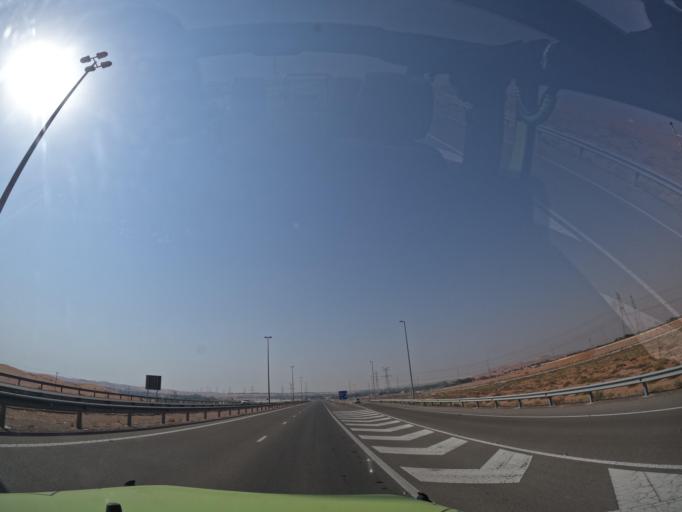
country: OM
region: Al Buraimi
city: Al Buraymi
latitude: 24.3729
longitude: 55.7284
